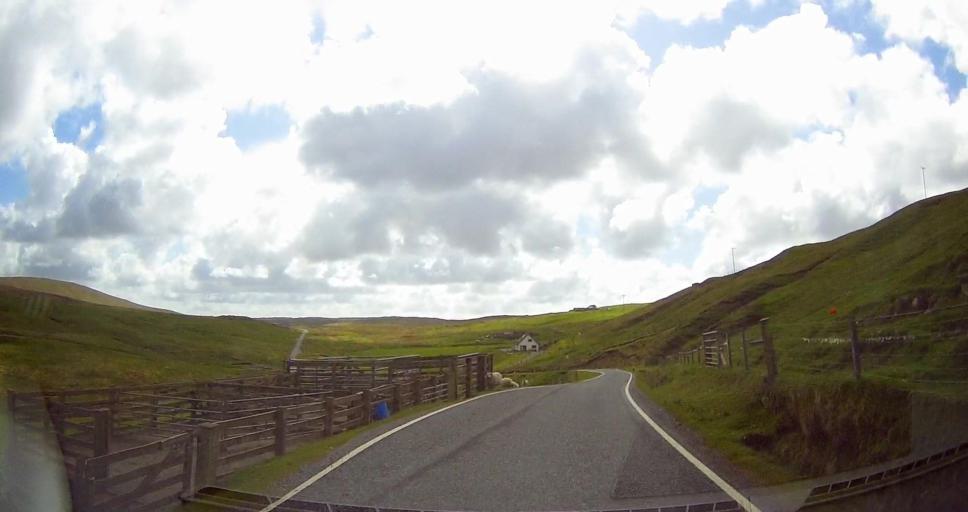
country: GB
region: Scotland
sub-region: Shetland Islands
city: Lerwick
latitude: 60.5268
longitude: -1.3699
